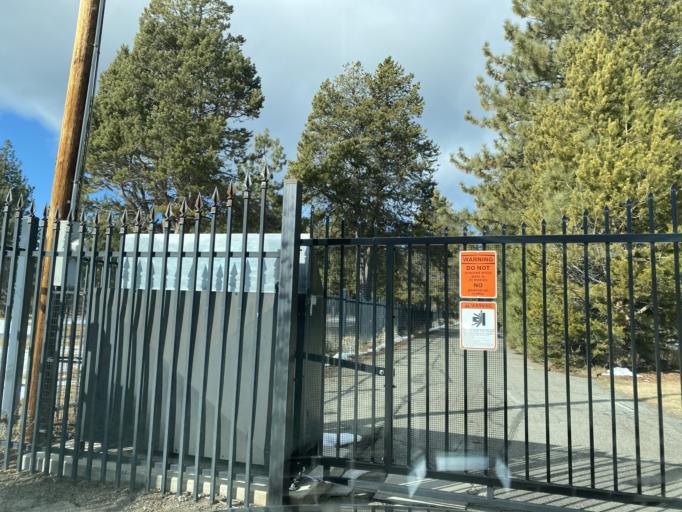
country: US
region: Nevada
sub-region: Douglas County
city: Kingsbury
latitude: 38.9701
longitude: -119.9403
